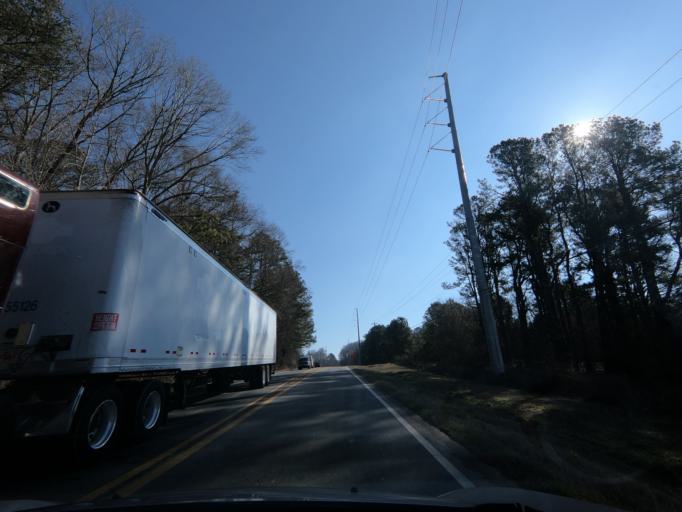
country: US
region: Georgia
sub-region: Forsyth County
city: Cumming
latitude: 34.3057
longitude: -84.2093
